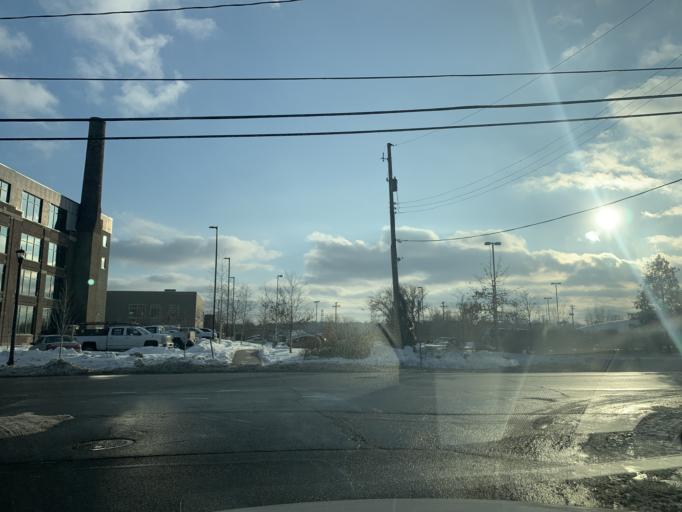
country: US
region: Minnesota
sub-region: Hennepin County
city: Minneapolis
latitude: 44.9804
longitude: -93.2931
